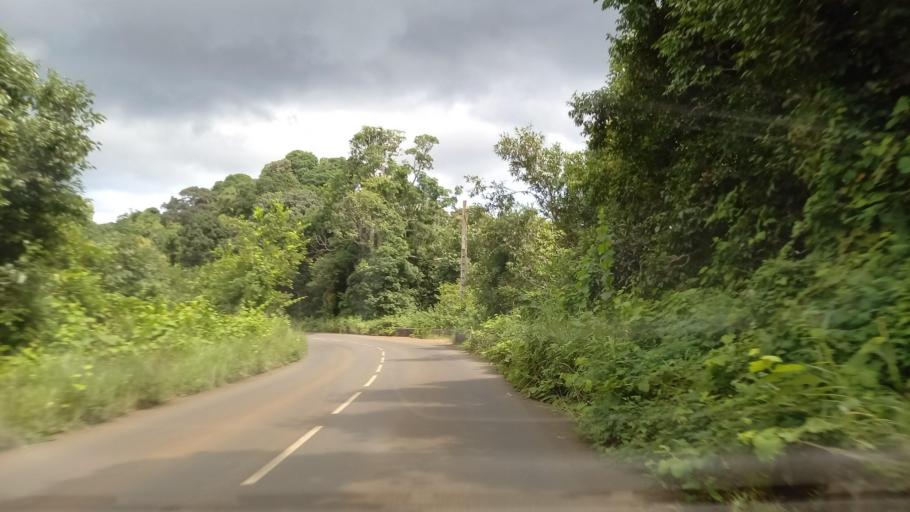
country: YT
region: Tsingoni
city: Tsingoni
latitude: -12.7881
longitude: 45.1605
